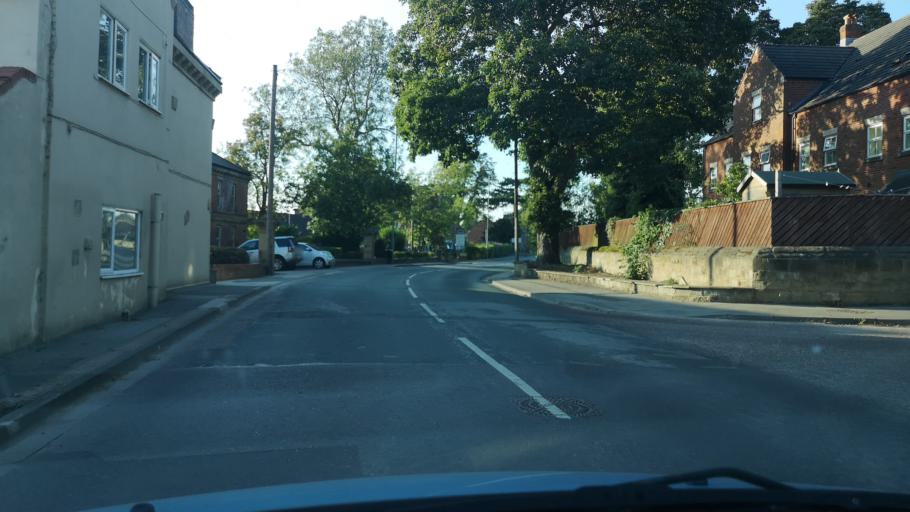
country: GB
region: England
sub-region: City and Borough of Wakefield
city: Pontefract
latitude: 53.6763
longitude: -1.2937
